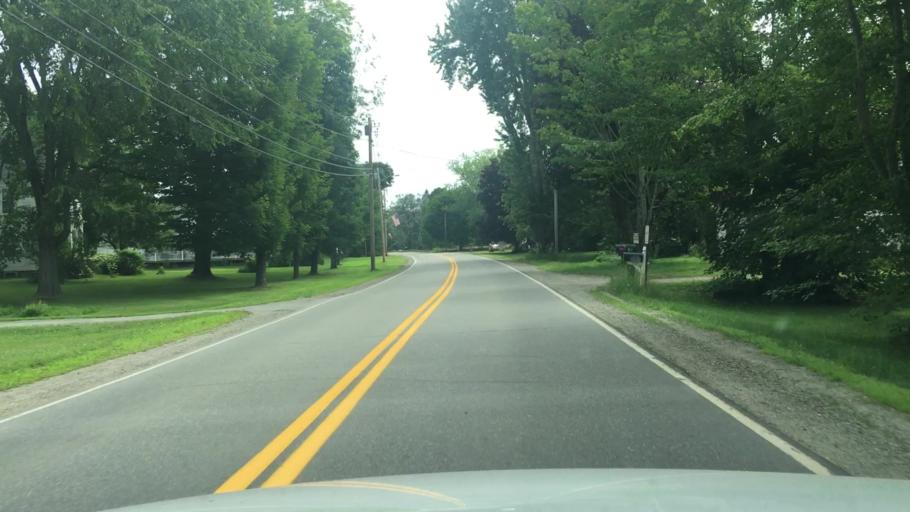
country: US
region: Maine
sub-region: Waldo County
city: Troy
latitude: 44.6135
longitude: -69.3283
